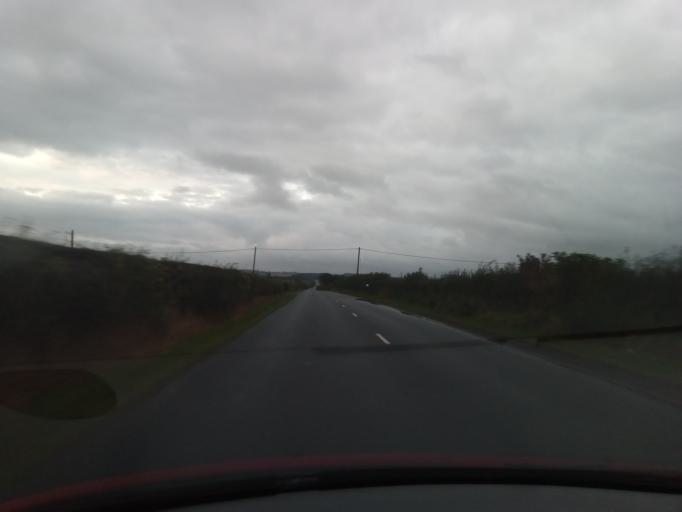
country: GB
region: England
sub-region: Darlington
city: Denton
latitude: 54.5518
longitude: -1.6748
